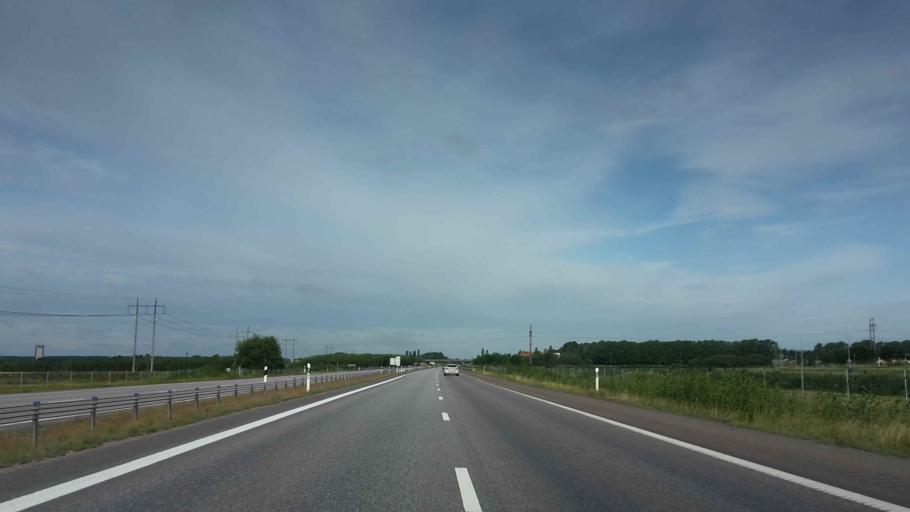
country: SE
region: OEstergoetland
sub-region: Linkopings Kommun
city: Ekangen
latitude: 58.4325
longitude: 15.6605
